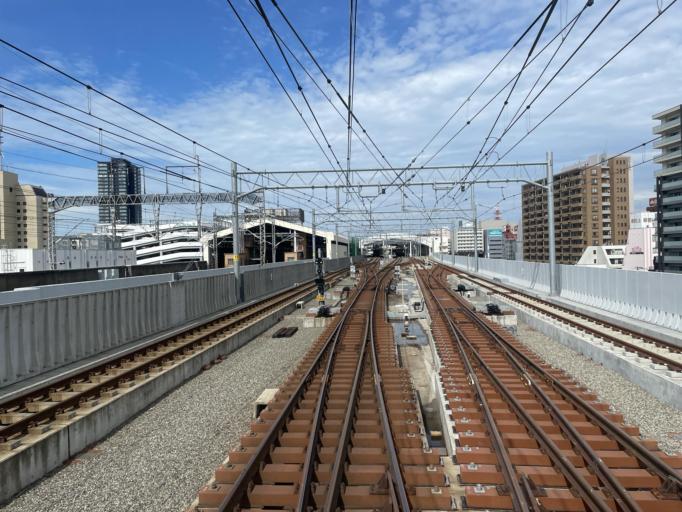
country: JP
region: Niigata
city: Niigata-shi
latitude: 37.9131
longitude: 139.0653
